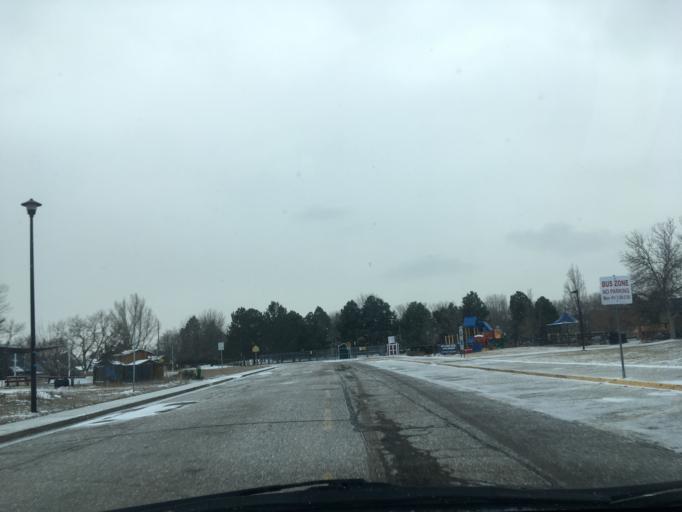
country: US
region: Colorado
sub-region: Boulder County
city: Lafayette
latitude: 39.9897
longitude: -105.0833
